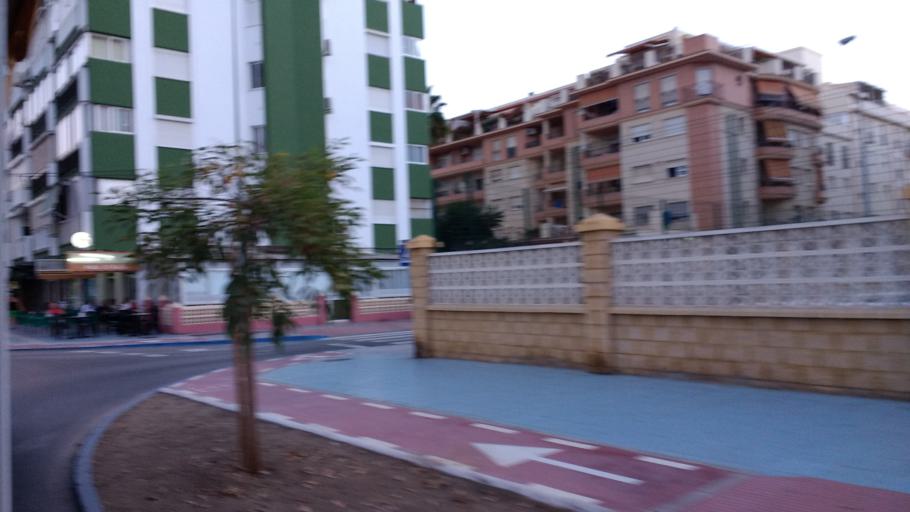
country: ES
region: Andalusia
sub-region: Provincia de Malaga
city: Velez-Malaga
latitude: 36.7373
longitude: -4.0983
